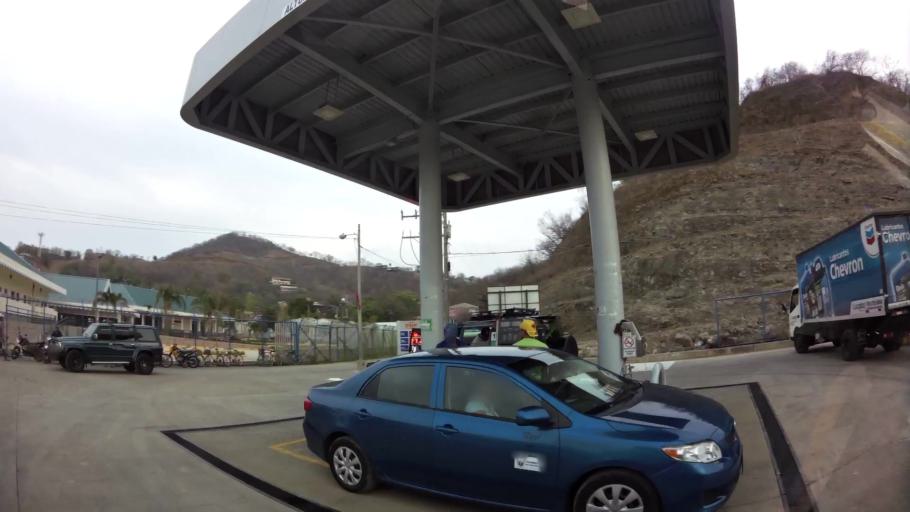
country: NI
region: Rivas
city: San Juan del Sur
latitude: 11.2506
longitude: -85.8756
